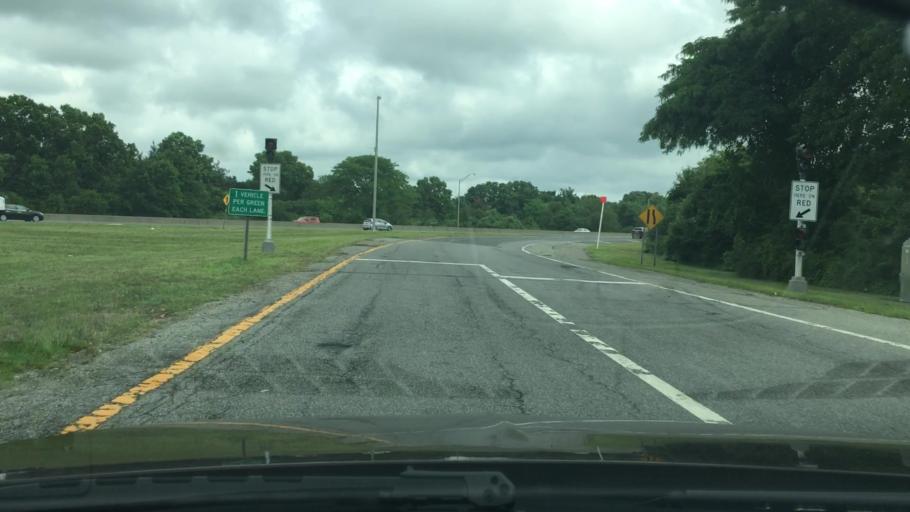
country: US
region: New York
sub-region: Suffolk County
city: Melville
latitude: 40.7803
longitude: -73.4156
